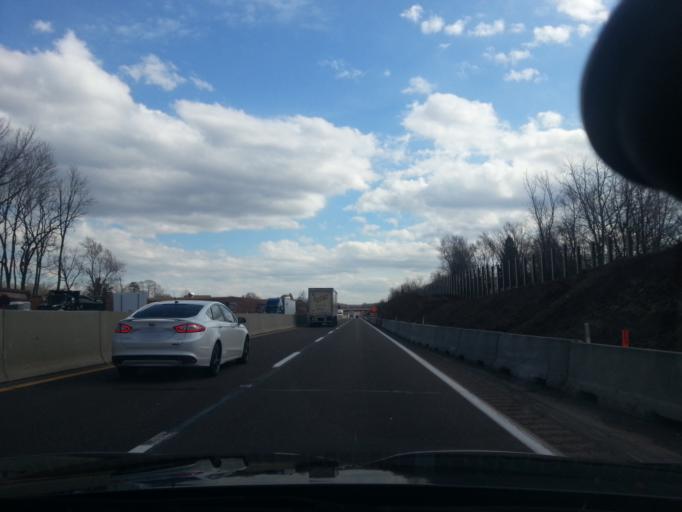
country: US
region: Pennsylvania
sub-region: Montgomery County
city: Kulpsville
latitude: 40.2321
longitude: -75.3367
